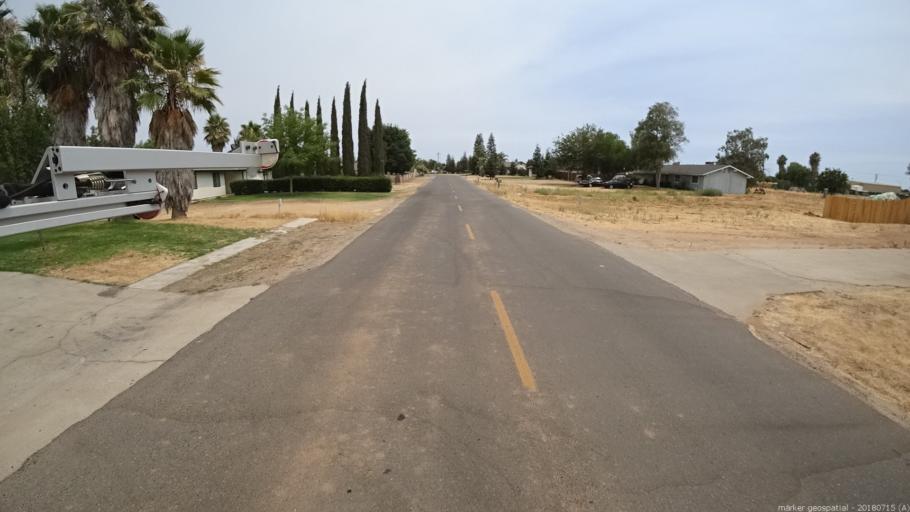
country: US
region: California
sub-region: Madera County
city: Madera Acres
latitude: 37.0035
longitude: -120.1039
